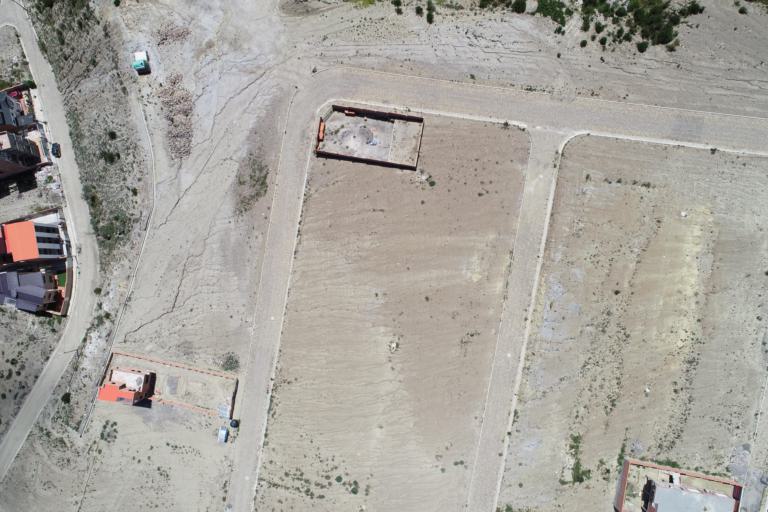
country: BO
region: La Paz
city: La Paz
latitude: -16.5222
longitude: -68.0488
